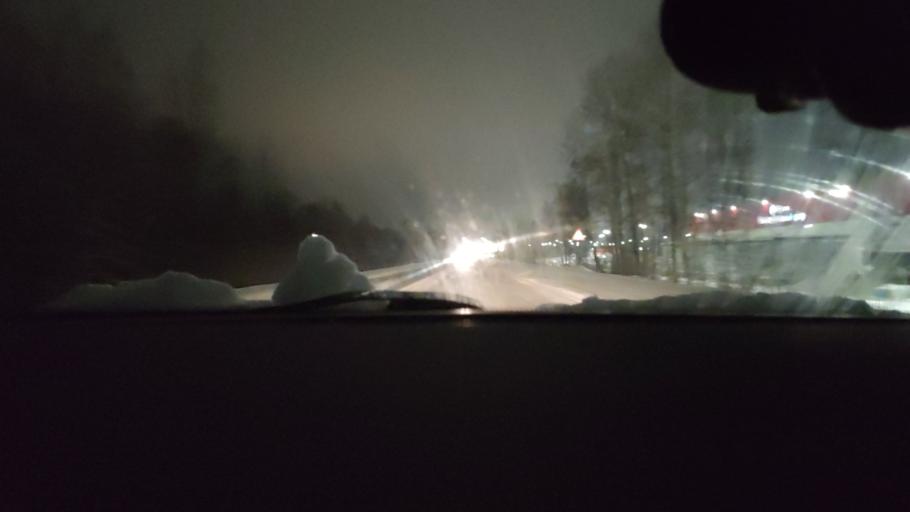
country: RU
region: Perm
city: Overyata
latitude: 58.0585
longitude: 55.8377
